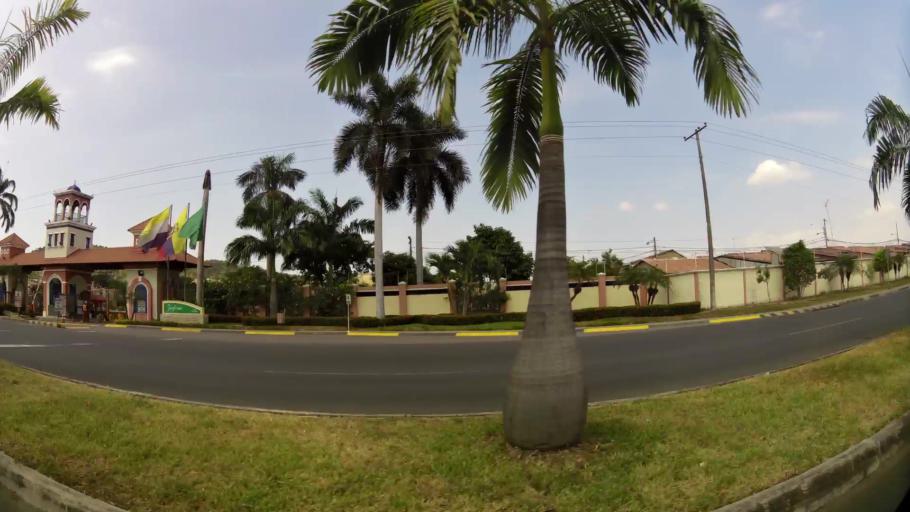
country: EC
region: Guayas
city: El Triunfo
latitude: -2.0430
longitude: -79.9148
